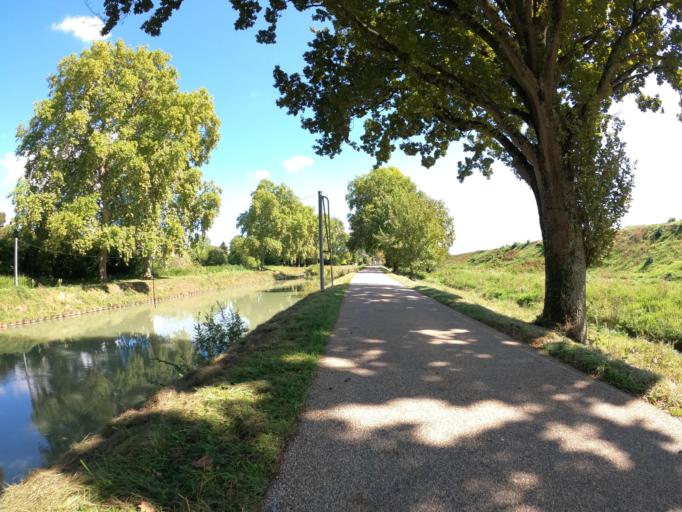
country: FR
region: Midi-Pyrenees
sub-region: Departement du Tarn-et-Garonne
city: Valence
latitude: 44.1041
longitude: 0.8981
